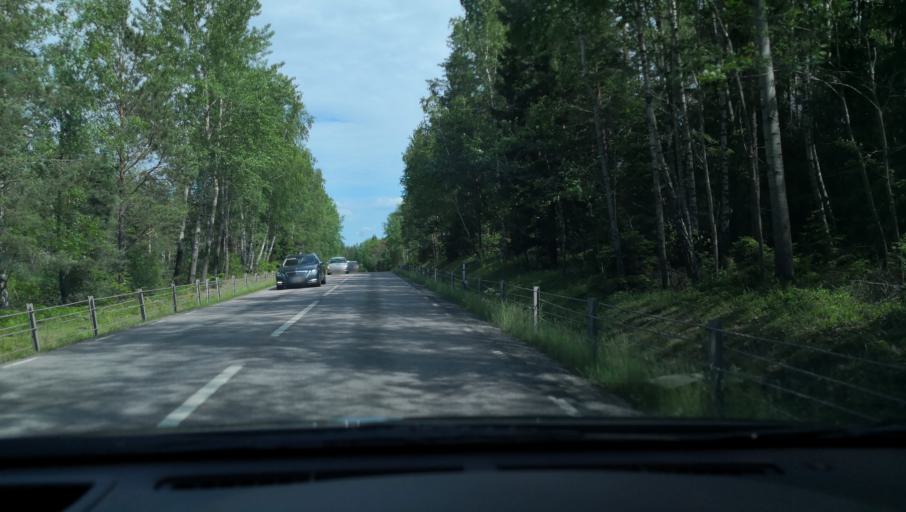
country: SE
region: Stockholm
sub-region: Sigtuna Kommun
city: Sigtuna
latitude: 59.6520
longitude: 17.6556
